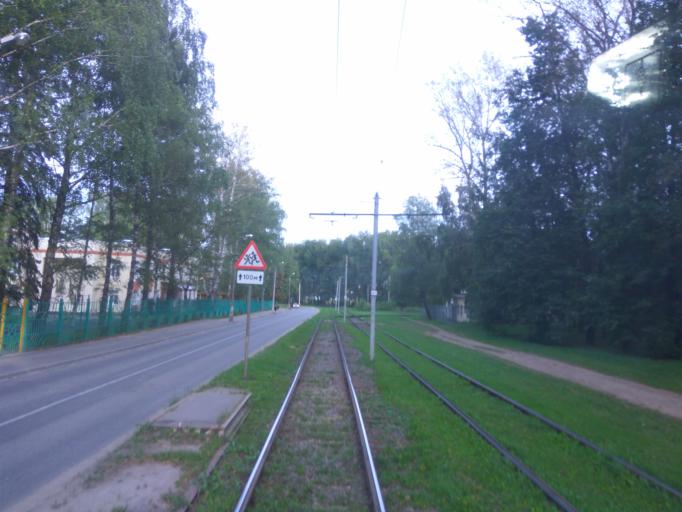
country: RU
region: Moskovskaya
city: Kolomna
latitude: 55.0743
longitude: 38.7850
